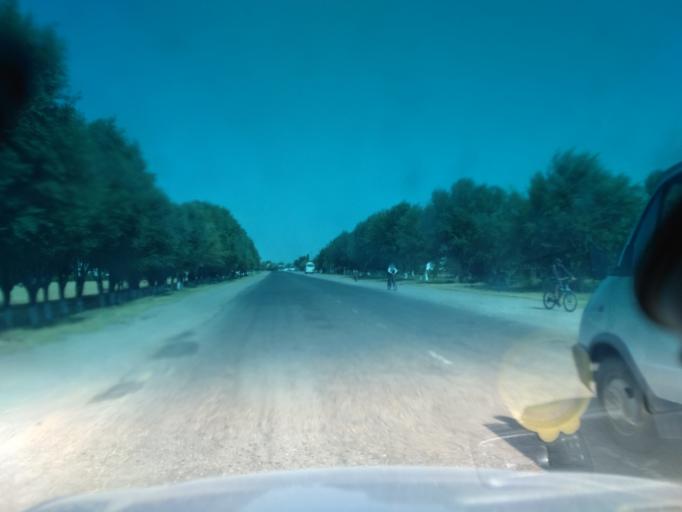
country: UZ
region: Sirdaryo
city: Guliston
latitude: 40.4866
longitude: 68.8952
